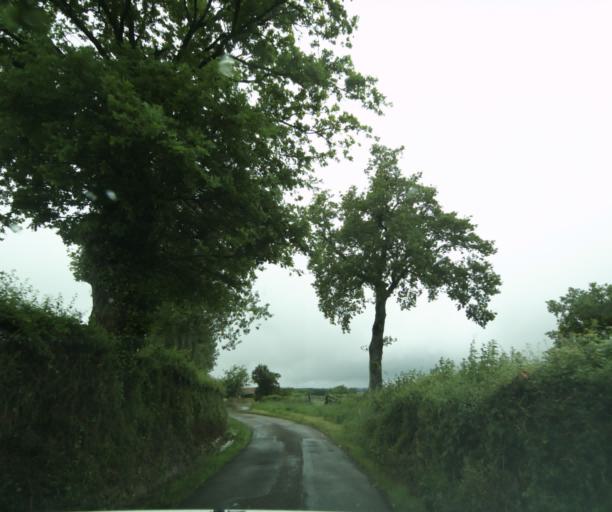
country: FR
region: Bourgogne
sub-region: Departement de Saone-et-Loire
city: Charolles
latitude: 46.3844
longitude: 4.2229
